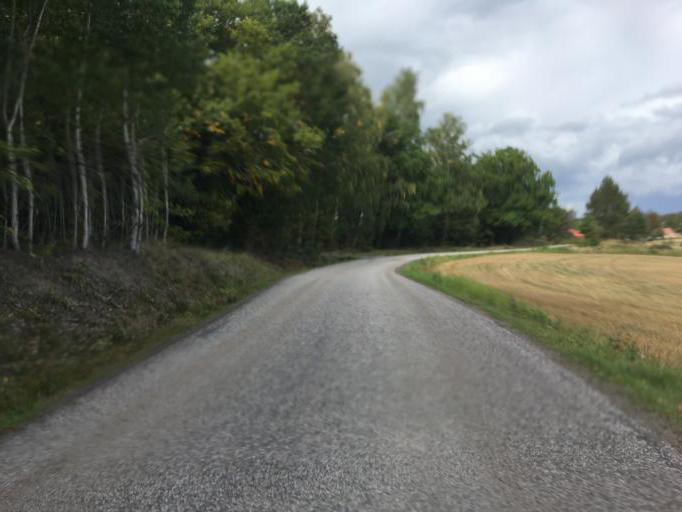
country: SE
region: Soedermanland
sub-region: Eskilstuna Kommun
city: Eskilstuna
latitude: 59.4442
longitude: 16.6399
